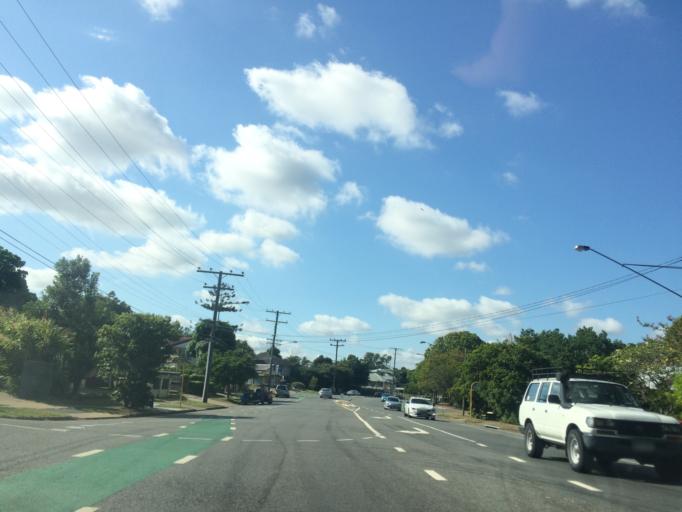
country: AU
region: Queensland
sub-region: Brisbane
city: Seven Hills
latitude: -27.4803
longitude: 153.0646
